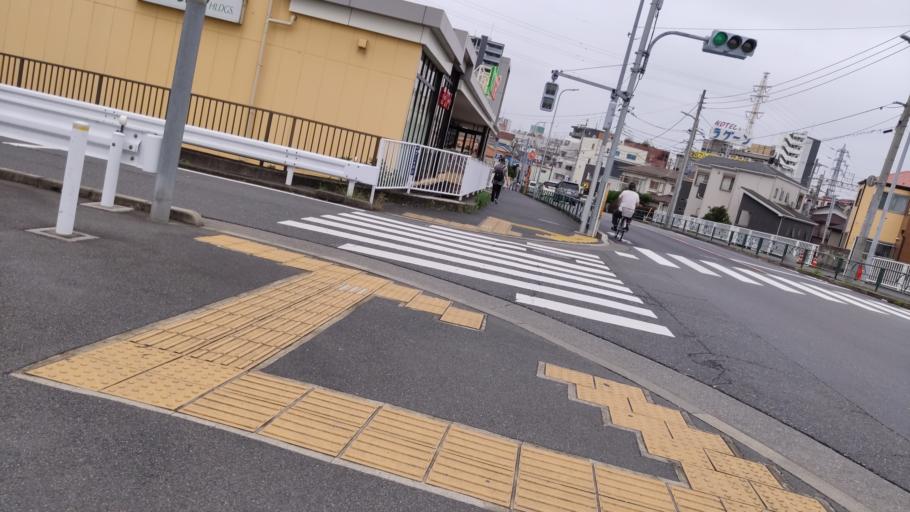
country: JP
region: Chiba
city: Matsudo
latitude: 35.7486
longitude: 139.8613
